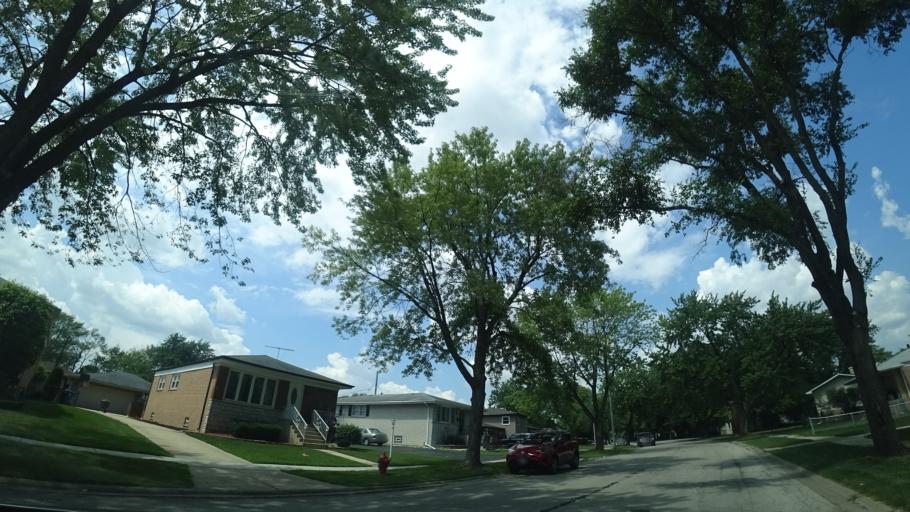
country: US
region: Illinois
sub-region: Cook County
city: Alsip
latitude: 41.6794
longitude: -87.7261
